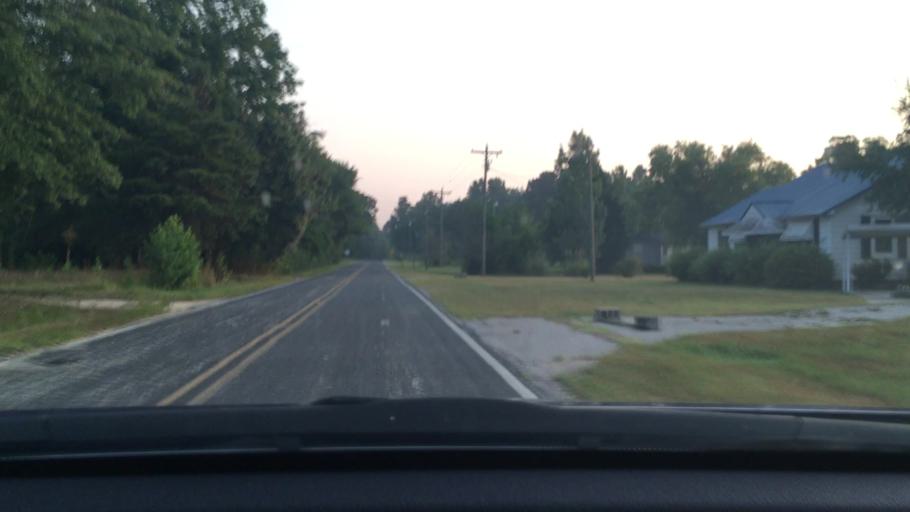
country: US
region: South Carolina
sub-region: Lee County
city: Bishopville
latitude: 34.2367
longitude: -80.1335
